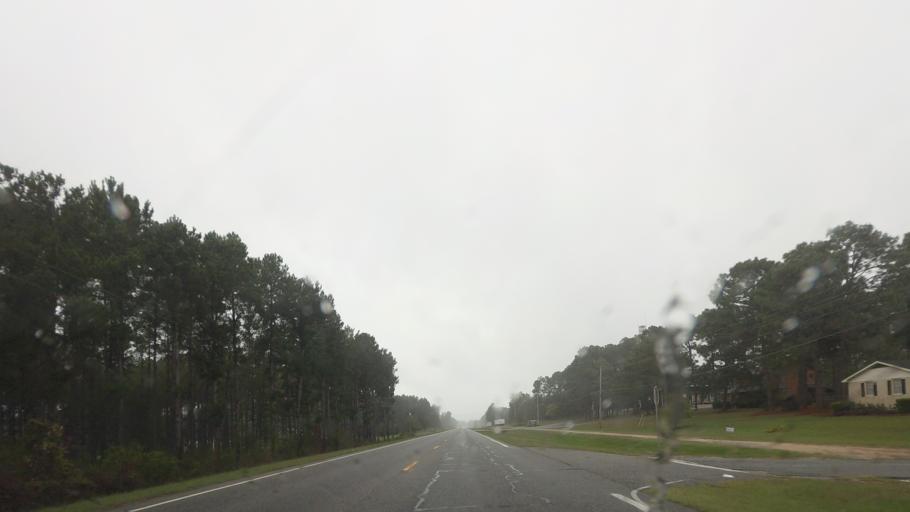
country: US
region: Georgia
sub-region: Ben Hill County
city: Fitzgerald
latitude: 31.7508
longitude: -83.2460
